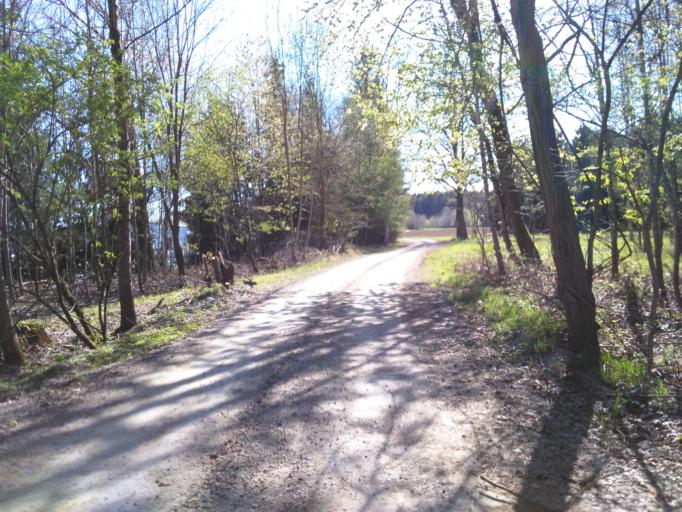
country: DE
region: Bavaria
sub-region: Upper Bavaria
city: Landsberied
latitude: 48.1979
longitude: 11.2037
